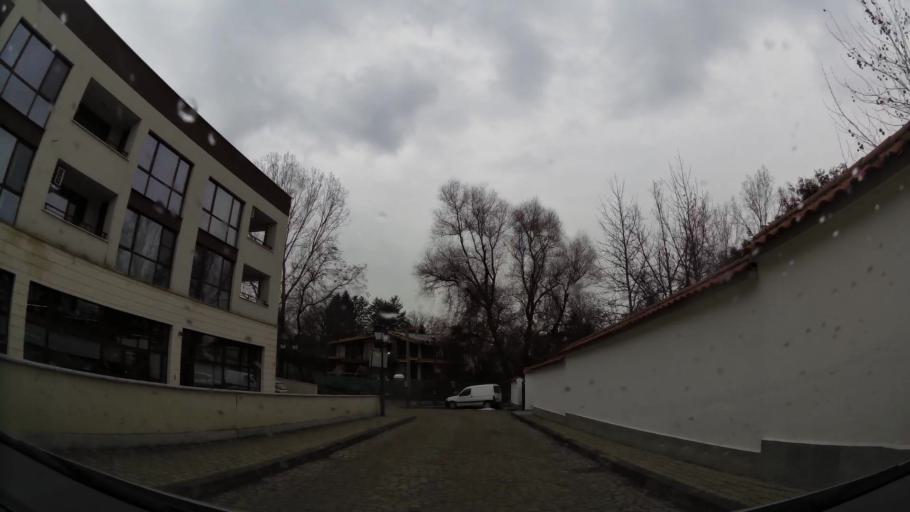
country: BG
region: Sofia-Capital
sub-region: Stolichna Obshtina
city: Sofia
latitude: 42.6162
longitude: 23.3759
